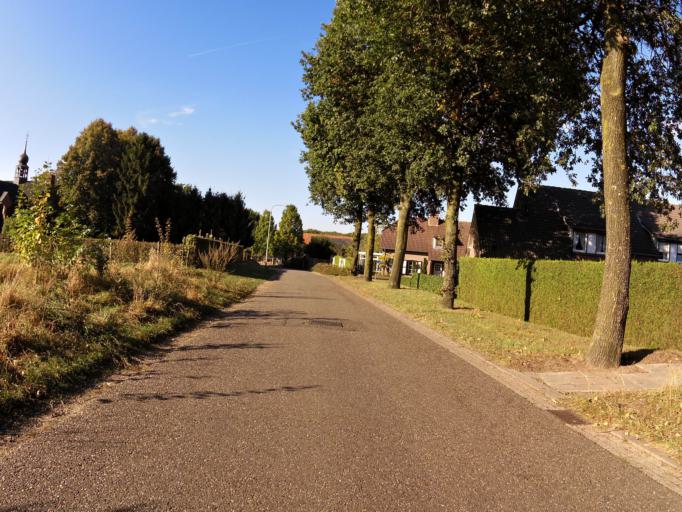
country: NL
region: Limburg
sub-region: Gemeente Bergen
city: Wellerlooi
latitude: 51.5341
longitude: 6.1380
